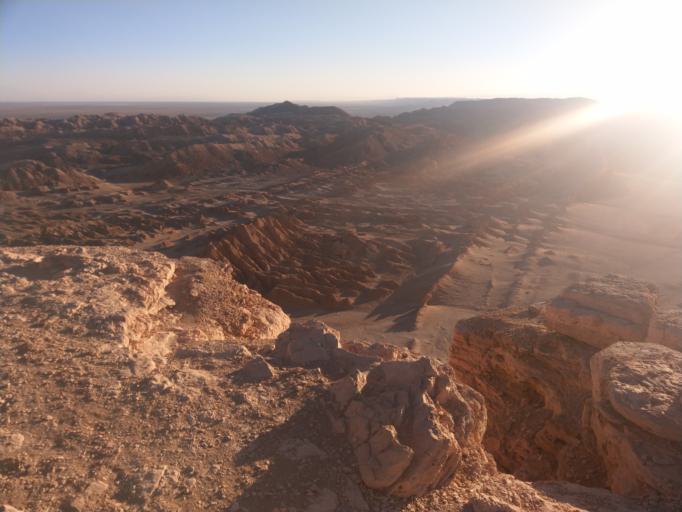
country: CL
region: Antofagasta
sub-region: Provincia de El Loa
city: San Pedro de Atacama
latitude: -22.9170
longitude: -68.2544
